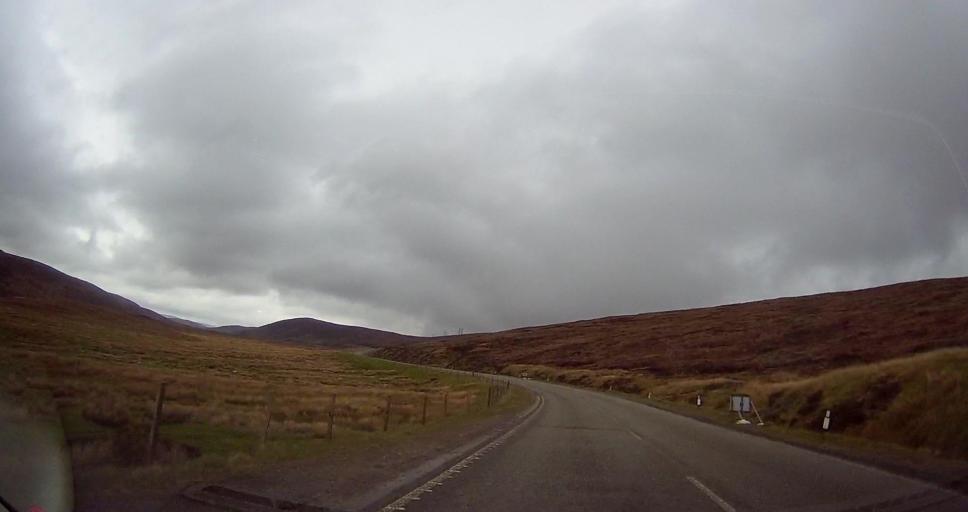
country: GB
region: Scotland
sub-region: Shetland Islands
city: Lerwick
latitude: 60.2855
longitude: -1.2421
